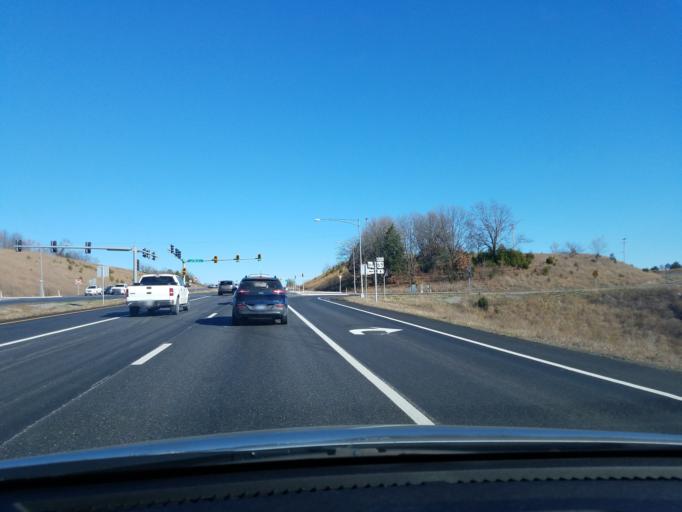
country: US
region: Missouri
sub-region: Taney County
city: Hollister
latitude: 36.5690
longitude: -93.2506
